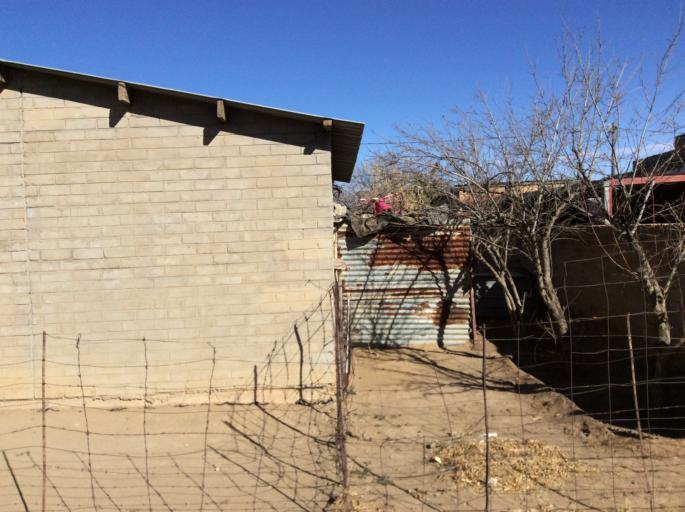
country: ZA
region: Orange Free State
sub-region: Lejweleputswa District Municipality
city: Brandfort
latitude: -28.7340
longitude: 26.1062
